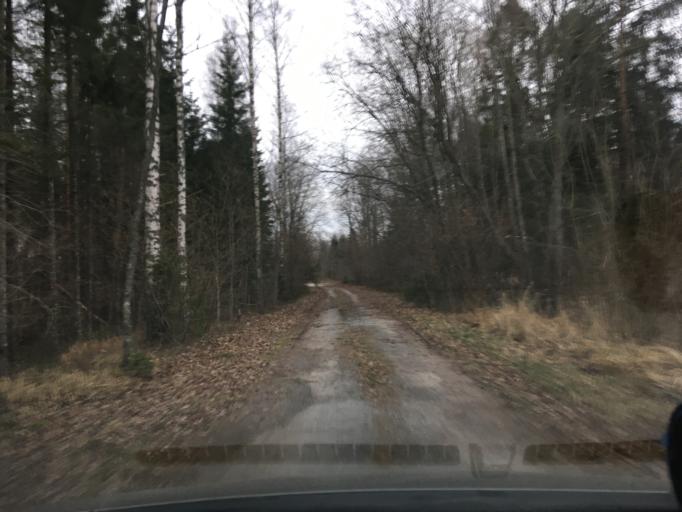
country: EE
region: Harju
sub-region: Nissi vald
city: Turba
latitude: 58.9734
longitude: 24.0627
